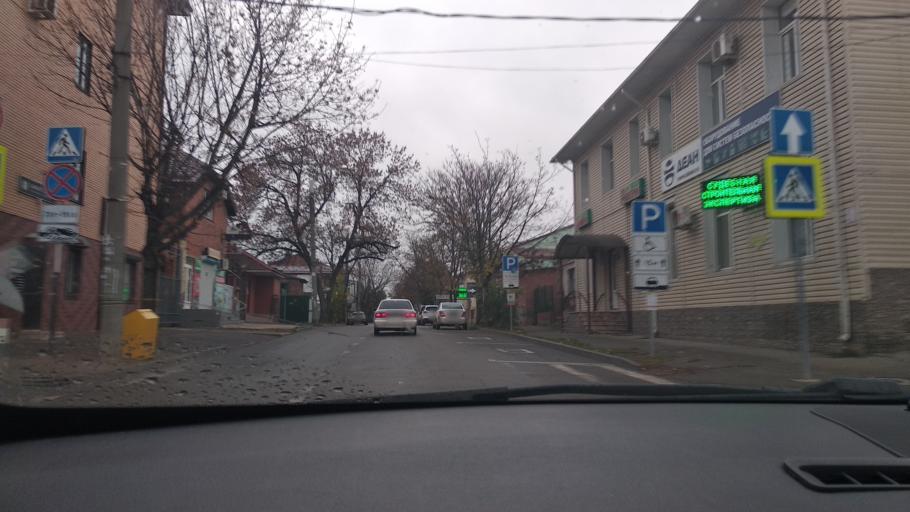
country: RU
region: Krasnodarskiy
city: Krasnodar
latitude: 45.0235
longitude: 38.9811
